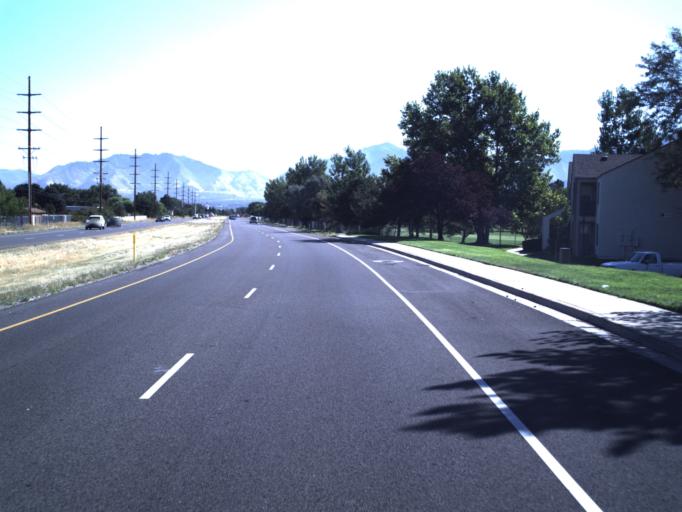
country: US
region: Utah
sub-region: Salt Lake County
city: Taylorsville
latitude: 40.6680
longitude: -111.9334
